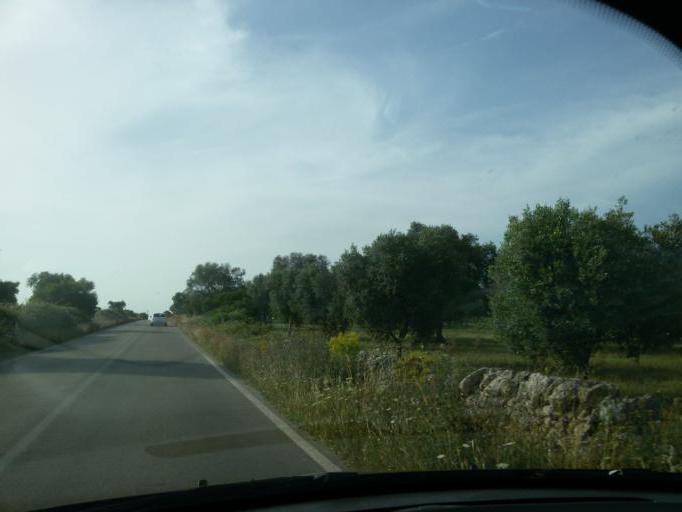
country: IT
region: Apulia
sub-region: Provincia di Lecce
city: Porto Cesareo
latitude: 40.3148
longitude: 17.8617
